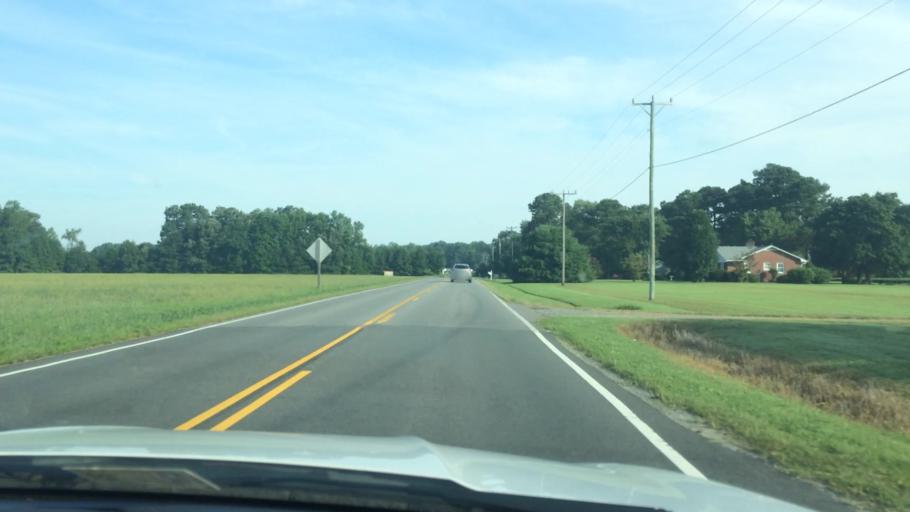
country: US
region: Virginia
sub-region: Middlesex County
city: Deltaville
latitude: 37.4974
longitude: -76.4117
